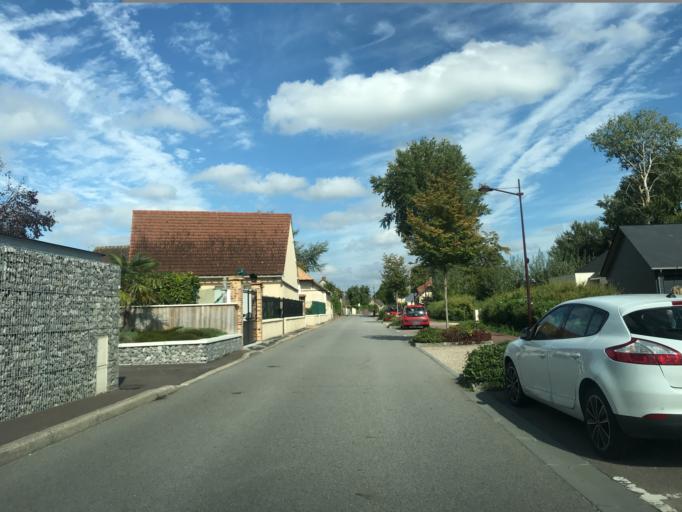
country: FR
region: Haute-Normandie
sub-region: Departement de l'Eure
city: Le Vaudreuil
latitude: 49.2535
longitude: 1.1988
